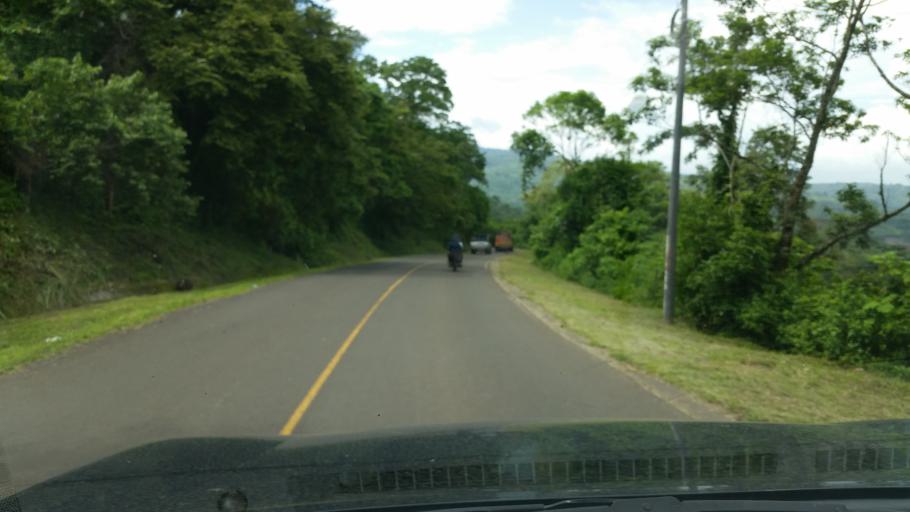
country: NI
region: Matagalpa
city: San Ramon
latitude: 12.9731
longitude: -85.8500
